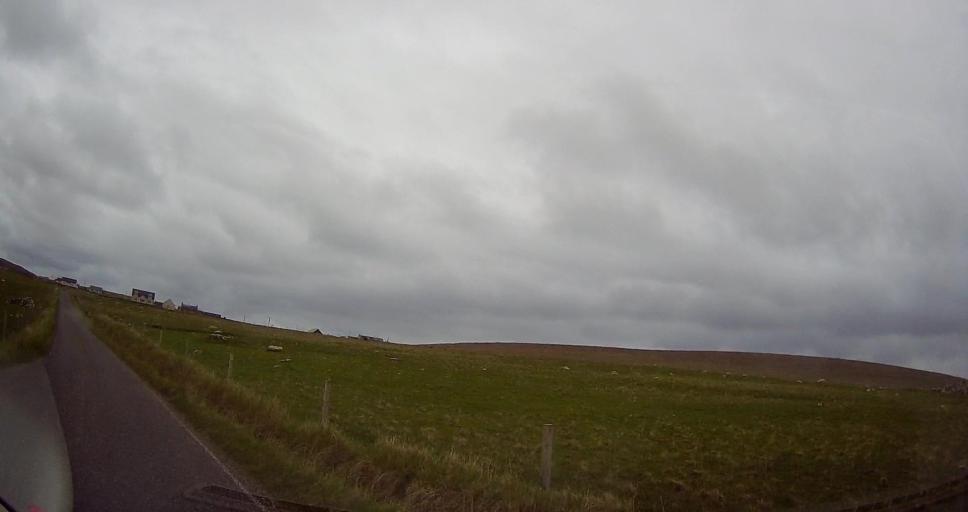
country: GB
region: Scotland
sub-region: Shetland Islands
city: Shetland
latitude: 60.7908
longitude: -0.8201
